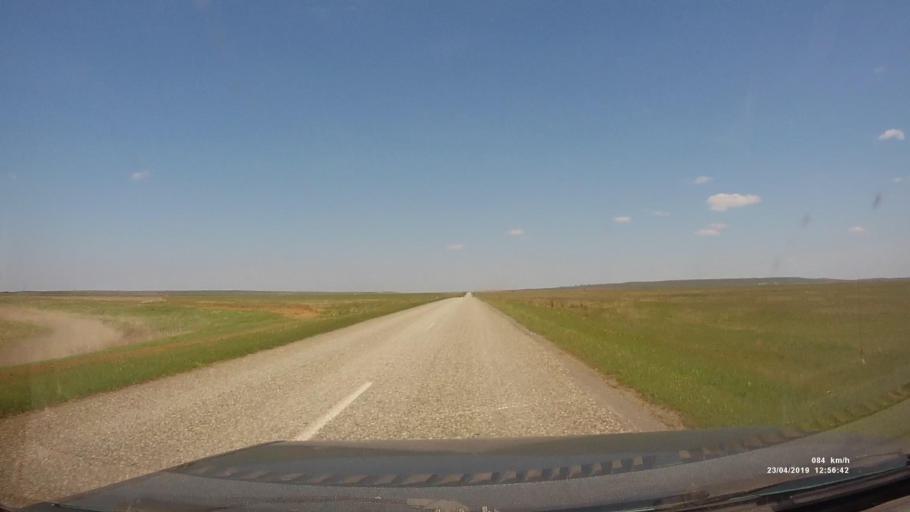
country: RU
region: Kalmykiya
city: Yashalta
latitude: 46.5965
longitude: 42.5740
